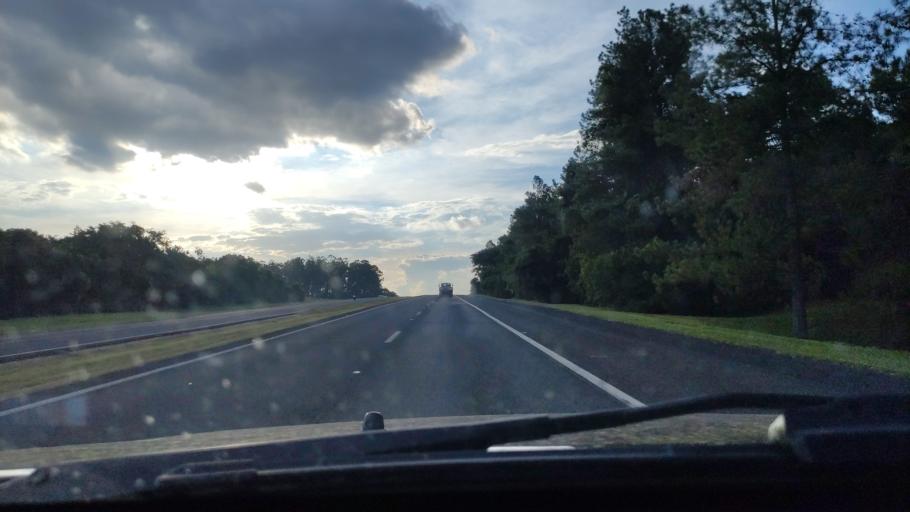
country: BR
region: Sao Paulo
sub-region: Rancharia
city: Rancharia
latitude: -22.4688
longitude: -50.9507
